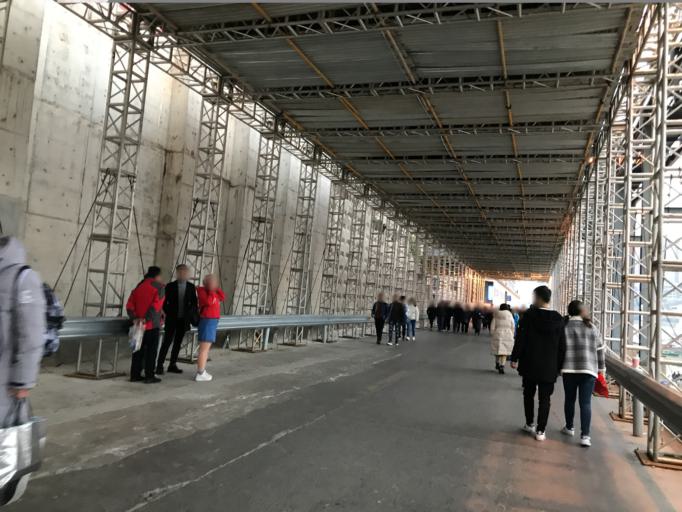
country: CN
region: Chongqing Shi
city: Nanping
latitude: 29.5683
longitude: 106.5853
